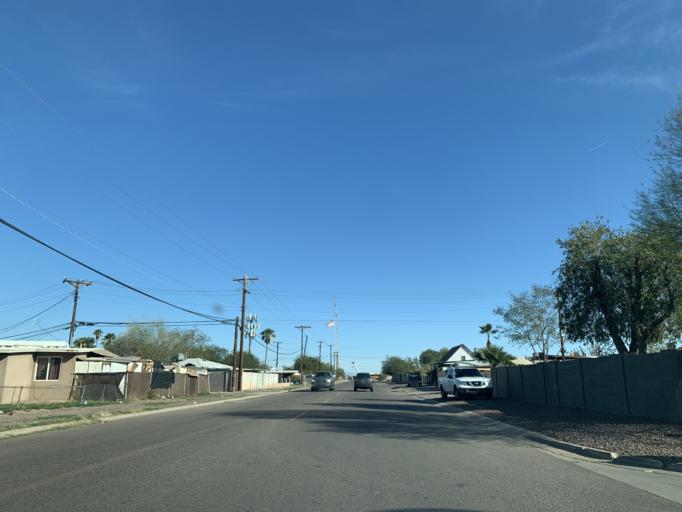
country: US
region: Arizona
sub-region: Maricopa County
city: Laveen
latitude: 33.4029
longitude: -112.1366
